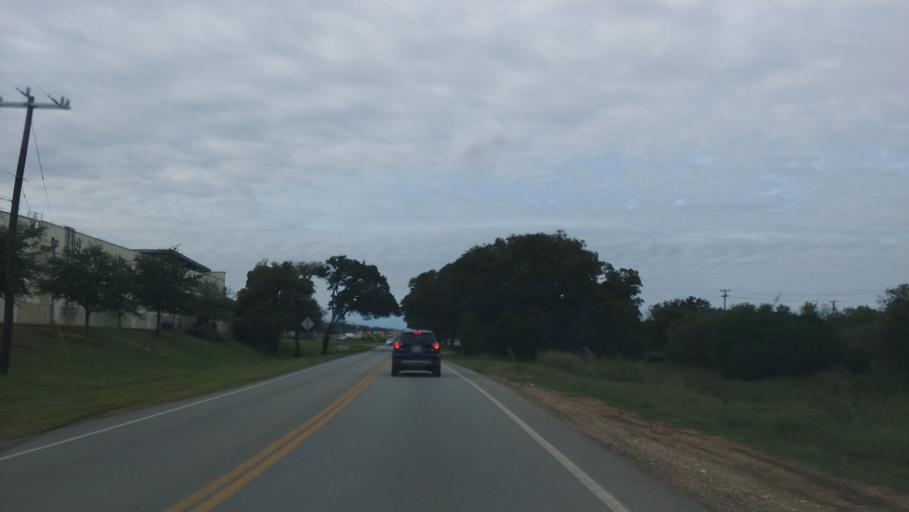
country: US
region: Texas
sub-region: Bexar County
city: Cross Mountain
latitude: 29.6682
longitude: -98.6307
